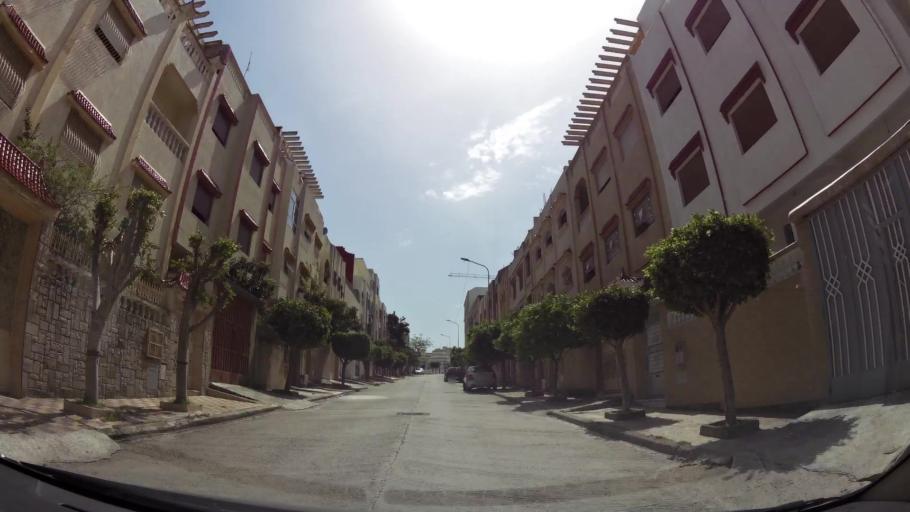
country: MA
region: Tanger-Tetouan
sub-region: Tanger-Assilah
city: Tangier
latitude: 35.7583
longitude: -5.8323
